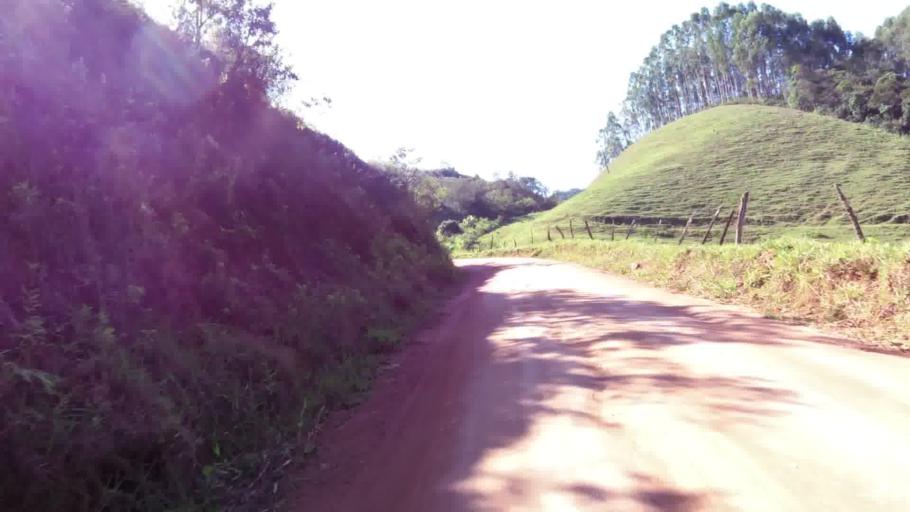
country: BR
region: Espirito Santo
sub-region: Alfredo Chaves
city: Alfredo Chaves
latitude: -20.5666
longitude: -40.7774
